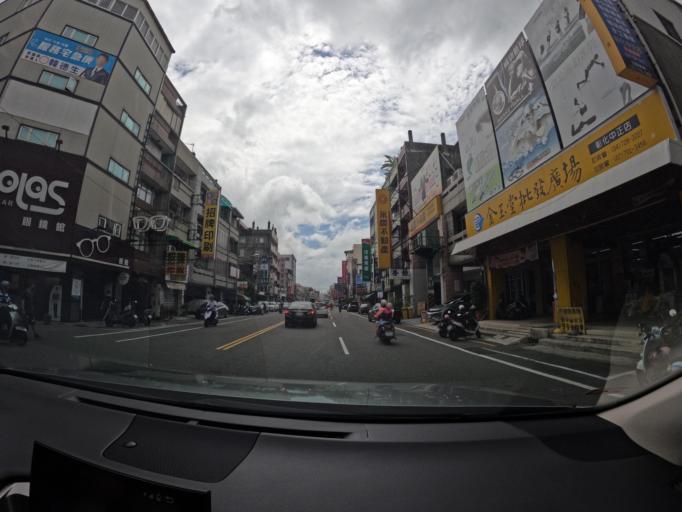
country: TW
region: Taiwan
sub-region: Changhua
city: Chang-hua
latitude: 24.0745
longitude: 120.5366
